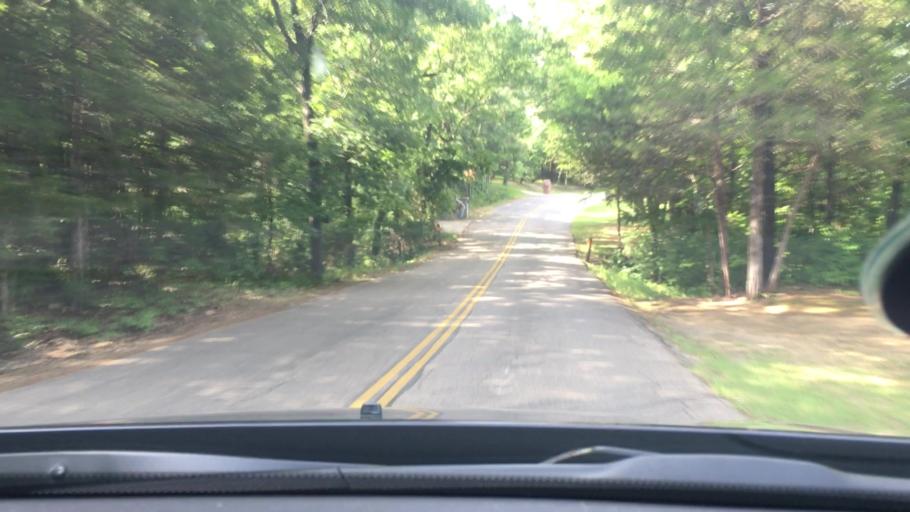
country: US
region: Oklahoma
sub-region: Pontotoc County
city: Ada
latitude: 34.7594
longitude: -96.6531
